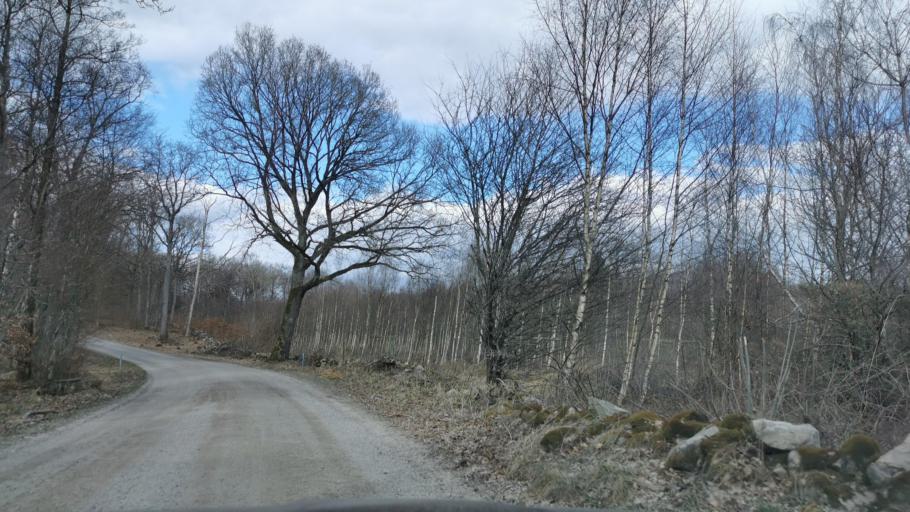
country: SE
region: Skane
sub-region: Sjobo Kommun
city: Sjoebo
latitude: 55.7439
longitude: 13.8381
